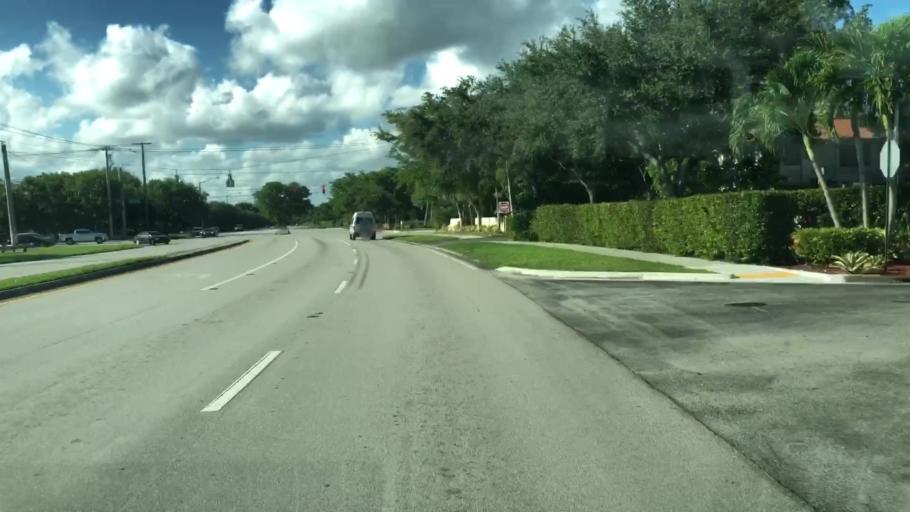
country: US
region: Florida
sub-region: Broward County
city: Coral Springs
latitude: 26.2598
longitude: -80.2662
